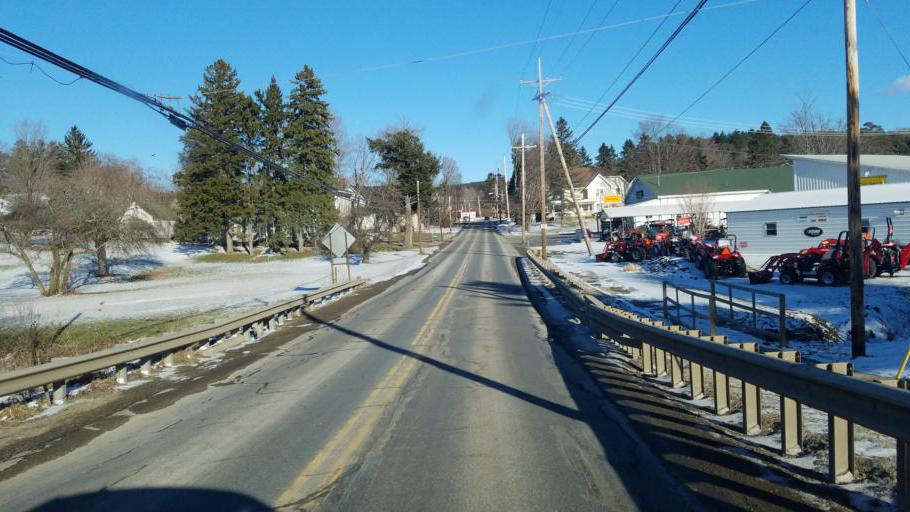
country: US
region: Pennsylvania
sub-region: Potter County
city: Galeton
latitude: 41.9040
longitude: -77.7661
